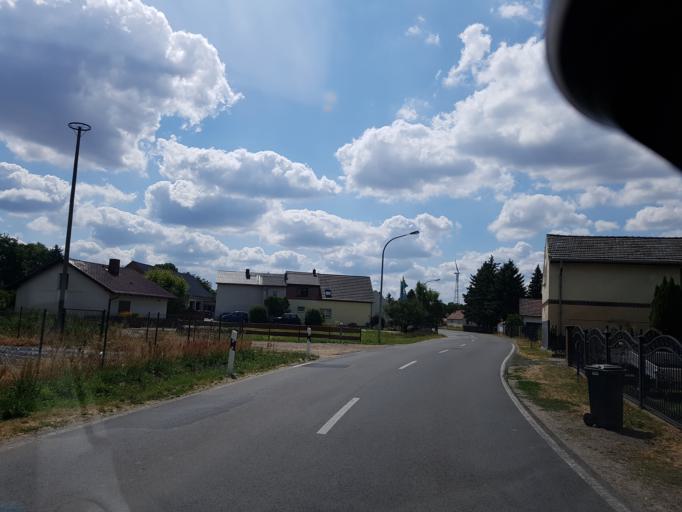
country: DE
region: Brandenburg
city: Drebkau
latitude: 51.6853
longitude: 14.2743
